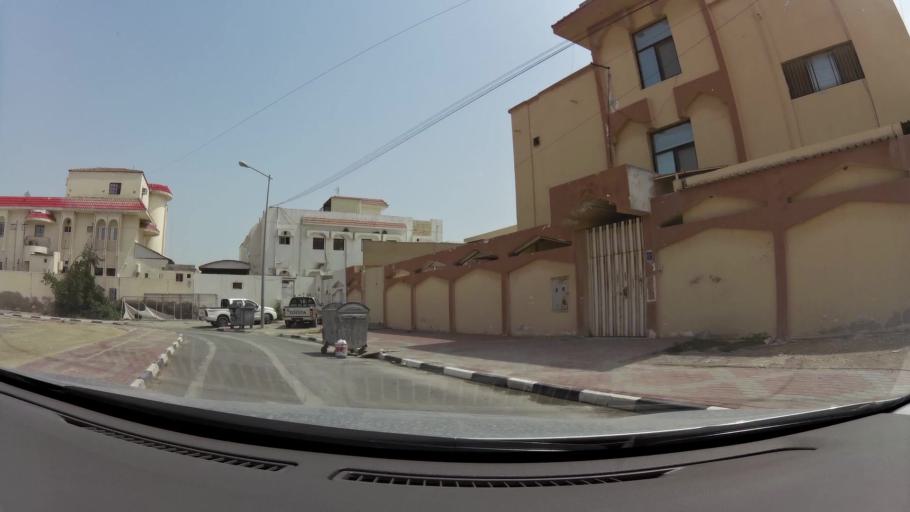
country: QA
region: Baladiyat ar Rayyan
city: Ar Rayyan
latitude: 25.2413
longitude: 51.4301
